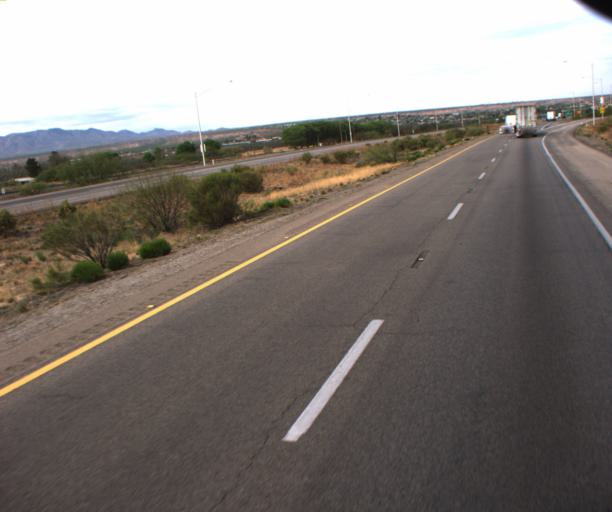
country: US
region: Arizona
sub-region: Cochise County
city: Benson
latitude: 31.9655
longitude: -110.2651
